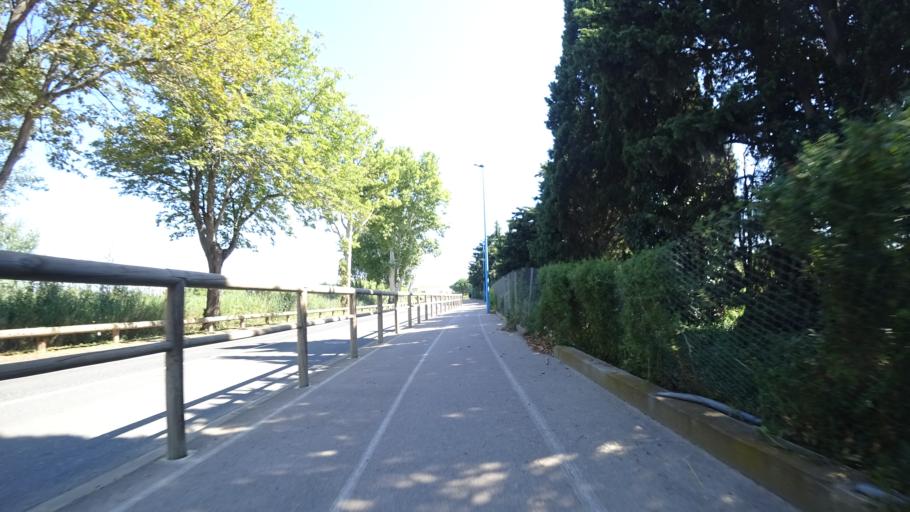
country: FR
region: Languedoc-Roussillon
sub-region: Departement des Pyrenees-Orientales
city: Sainte-Marie-Plage
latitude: 42.7279
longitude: 3.0118
